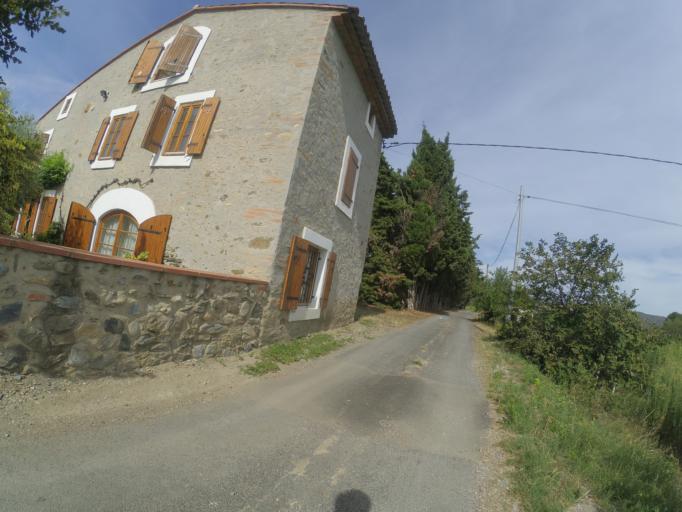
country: FR
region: Languedoc-Roussillon
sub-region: Departement des Pyrenees-Orientales
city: Ille-sur-Tet
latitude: 42.6600
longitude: 2.6278
